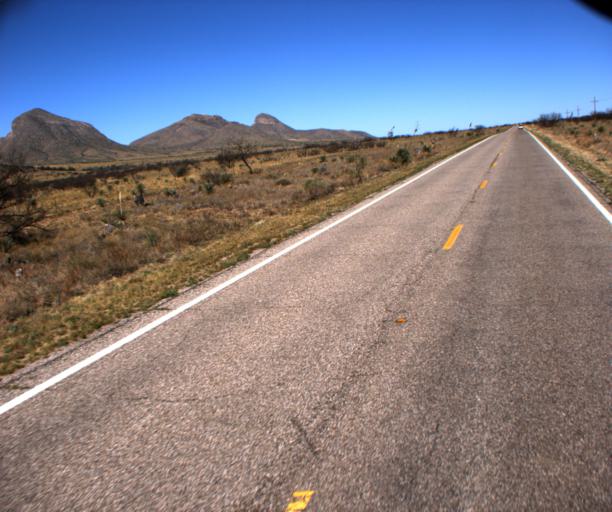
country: US
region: Arizona
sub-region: Cochise County
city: Huachuca City
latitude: 31.7016
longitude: -110.4315
